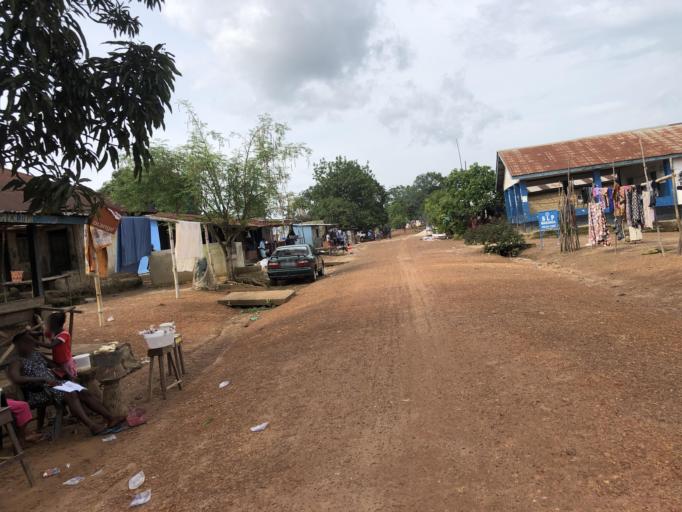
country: SL
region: Northern Province
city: Masaka
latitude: 8.7484
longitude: -11.8396
